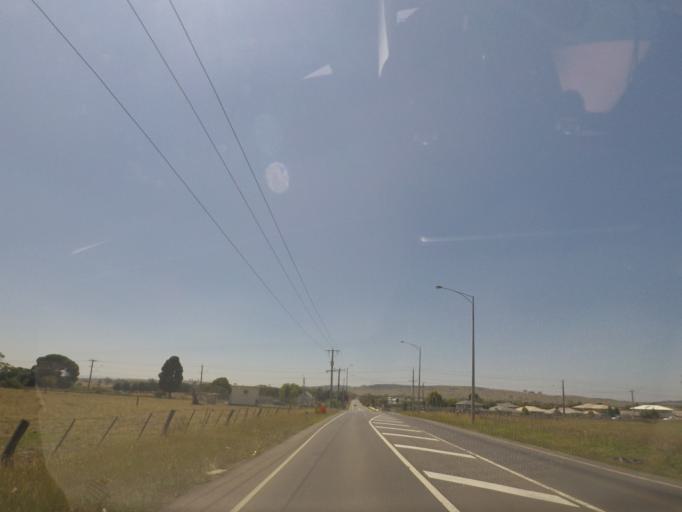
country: AU
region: Victoria
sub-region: Whittlesea
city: Epping
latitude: -37.6083
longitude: 145.0299
